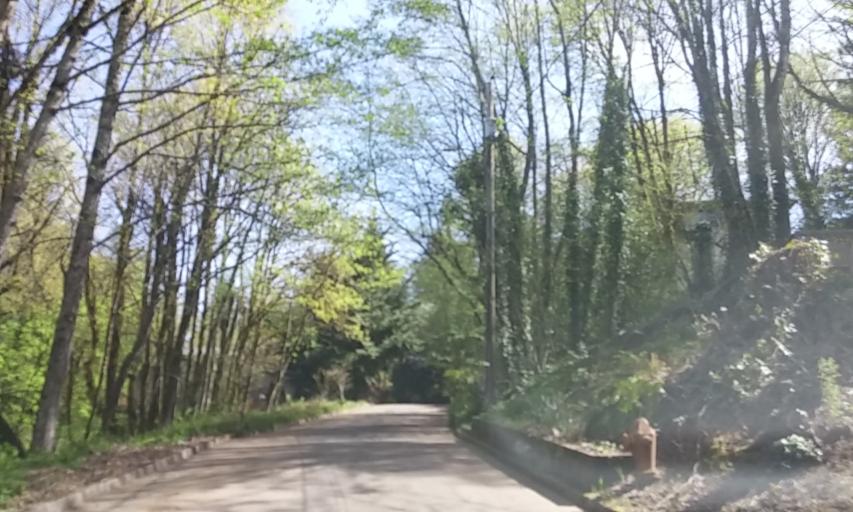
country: US
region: Oregon
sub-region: Washington County
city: West Haven-Sylvan
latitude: 45.5166
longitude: -122.7386
